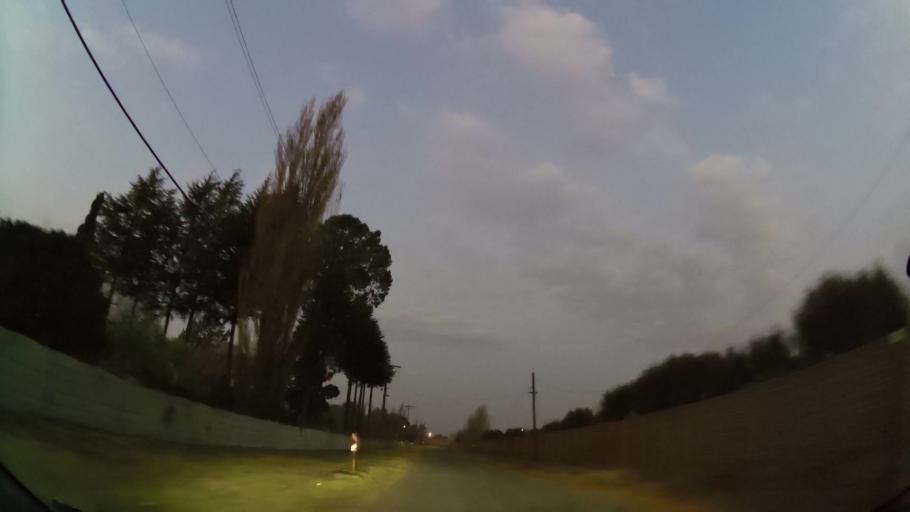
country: ZA
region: Gauteng
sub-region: Ekurhuleni Metropolitan Municipality
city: Benoni
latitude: -26.1089
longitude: 28.3166
